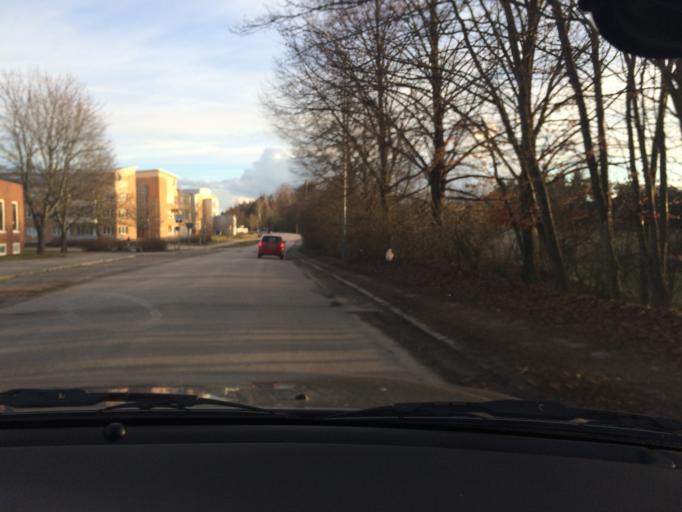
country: SE
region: Vaestmanland
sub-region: Vasteras
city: Vasteras
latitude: 59.6216
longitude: 16.5890
